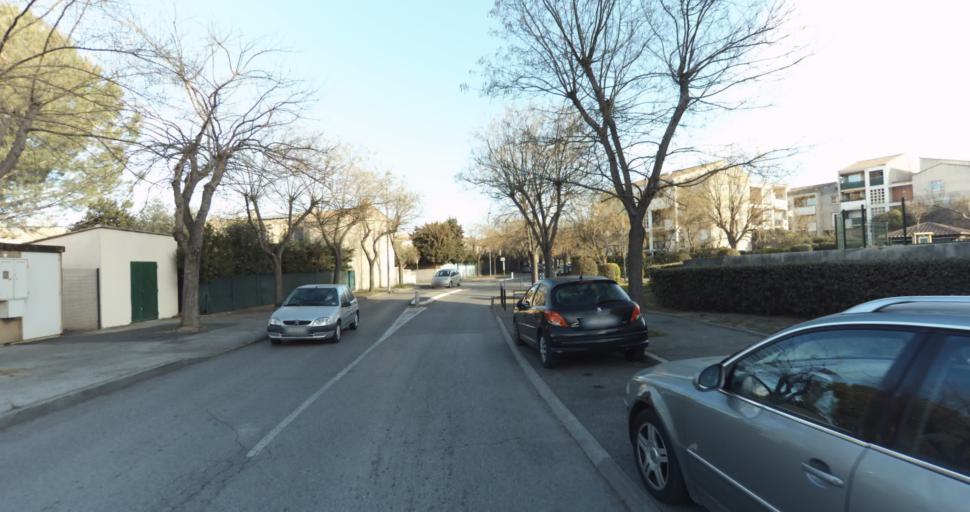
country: FR
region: Provence-Alpes-Cote d'Azur
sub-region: Departement des Bouches-du-Rhone
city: Aix-en-Provence
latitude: 43.5285
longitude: 5.4106
